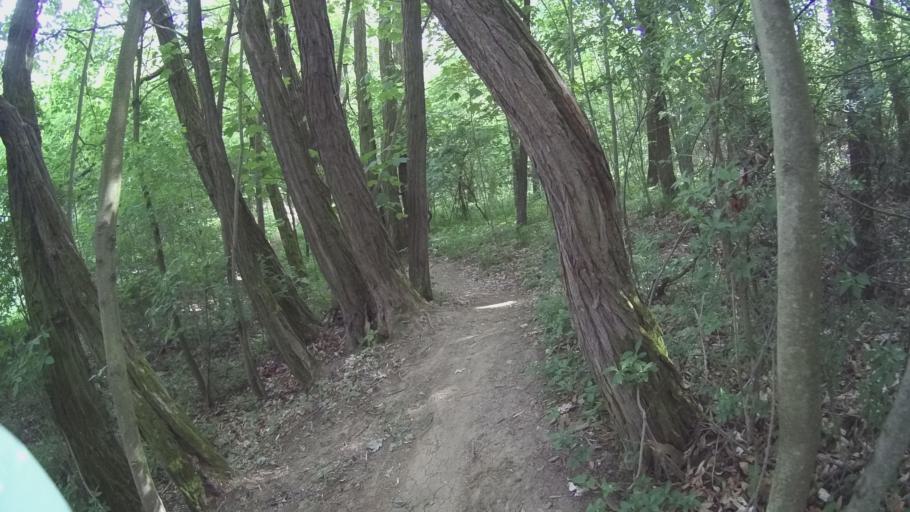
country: CZ
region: Central Bohemia
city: Zdiby
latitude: 50.2079
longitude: 14.4477
